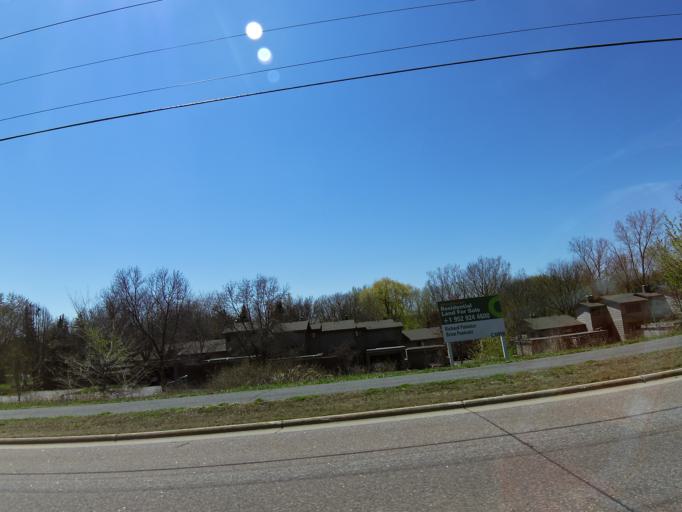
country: US
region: Minnesota
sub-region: Hennepin County
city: Eden Prairie
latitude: 44.8283
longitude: -93.4250
